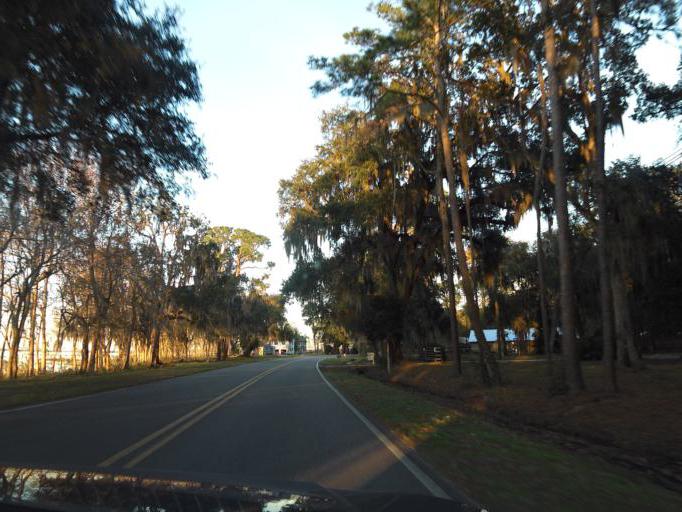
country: US
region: Florida
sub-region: Clay County
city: Green Cove Springs
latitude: 29.9223
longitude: -81.5934
